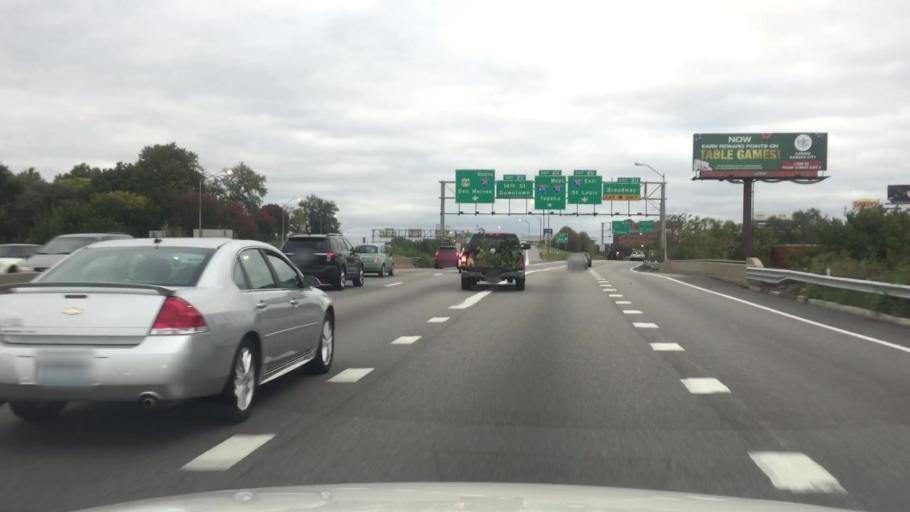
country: US
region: Missouri
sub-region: Jackson County
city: Kansas City
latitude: 39.0925
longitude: -94.5908
